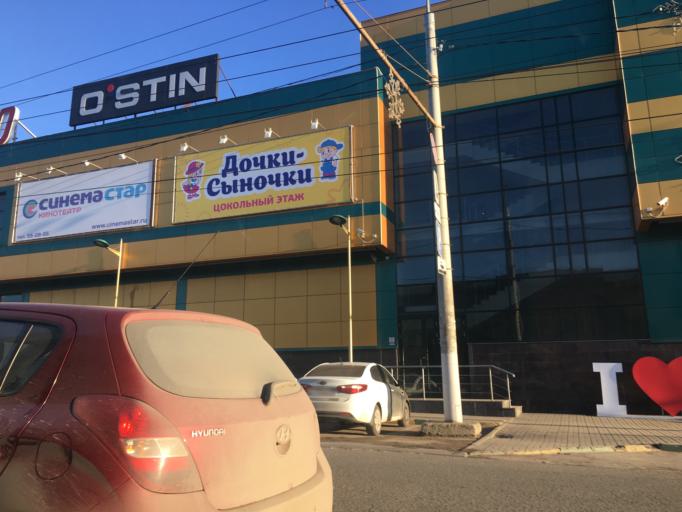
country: RU
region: Tula
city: Tula
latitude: 54.1998
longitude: 37.6365
